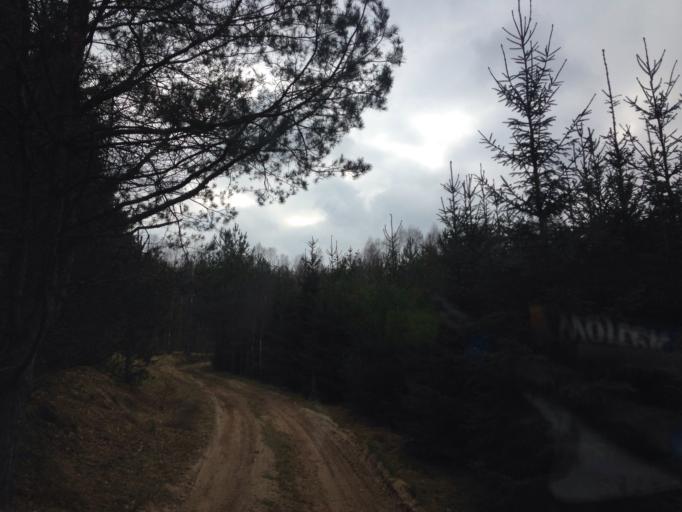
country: PL
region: Warmian-Masurian Voivodeship
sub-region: Powiat dzialdowski
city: Lidzbark
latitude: 53.3746
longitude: 19.7638
